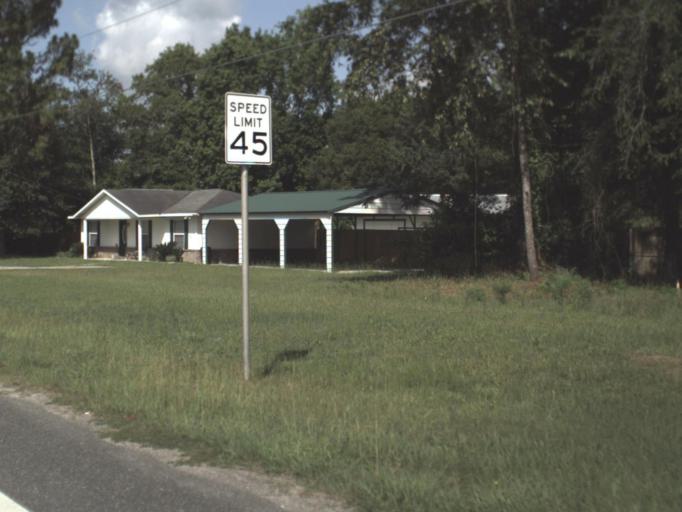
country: US
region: Florida
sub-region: Columbia County
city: Lake City
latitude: 30.1203
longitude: -82.7263
